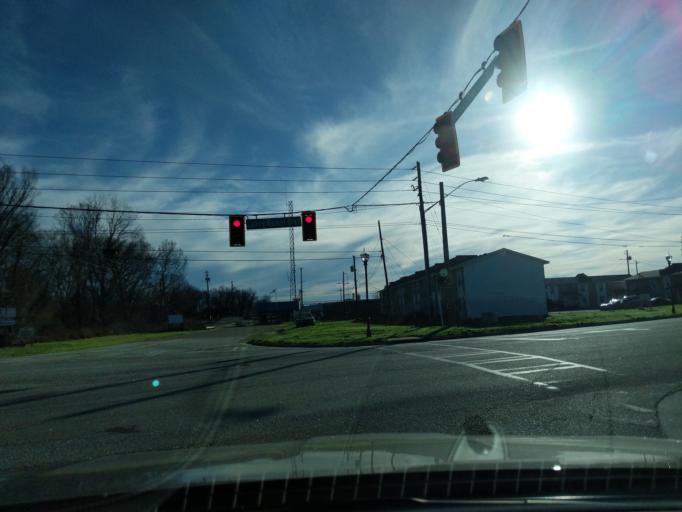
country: US
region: Georgia
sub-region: Richmond County
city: Augusta
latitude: 33.4577
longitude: -81.9538
